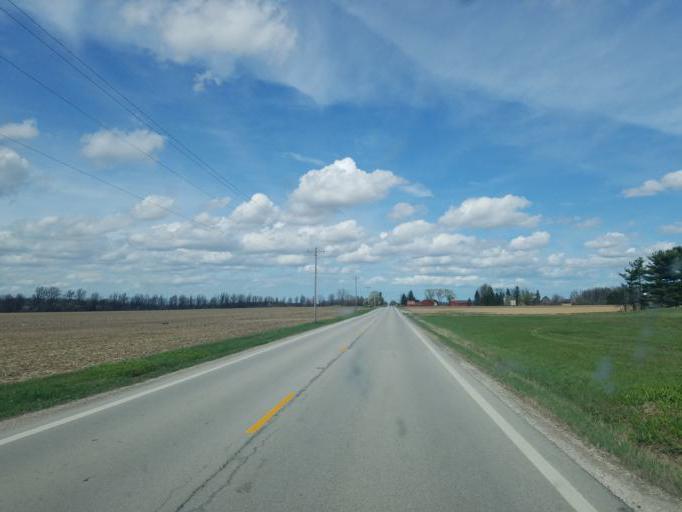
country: US
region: Ohio
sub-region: Huron County
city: Bellevue
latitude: 41.2158
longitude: -82.8174
